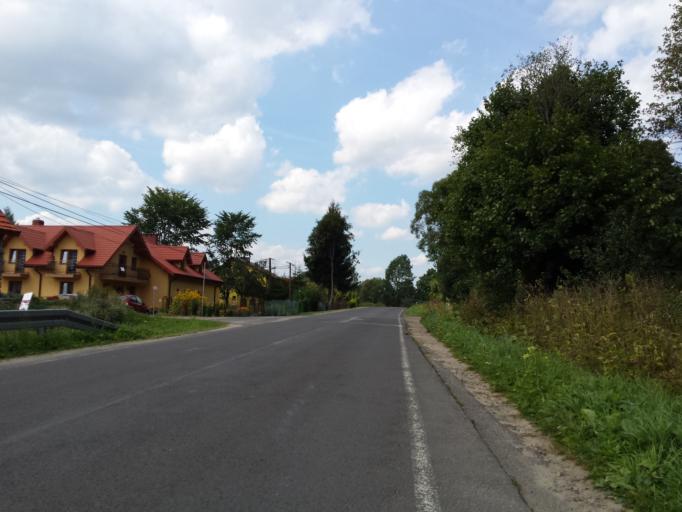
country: PL
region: Subcarpathian Voivodeship
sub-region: Powiat leski
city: Cisna
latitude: 49.1517
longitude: 22.4730
